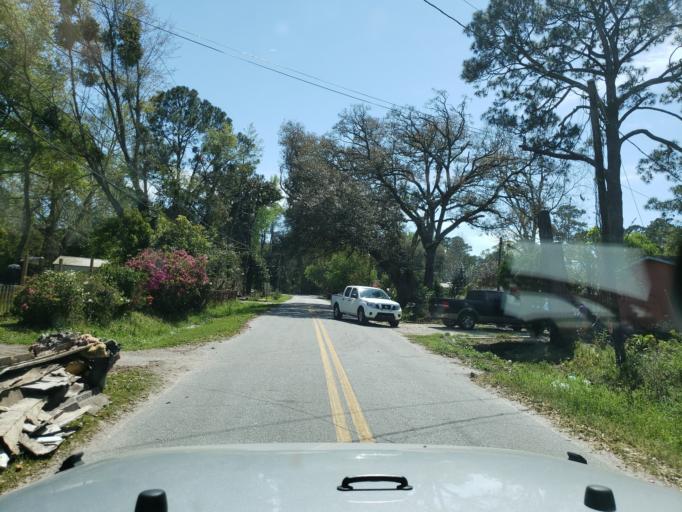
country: US
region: Georgia
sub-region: Chatham County
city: Montgomery
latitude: 31.9484
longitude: -81.1132
